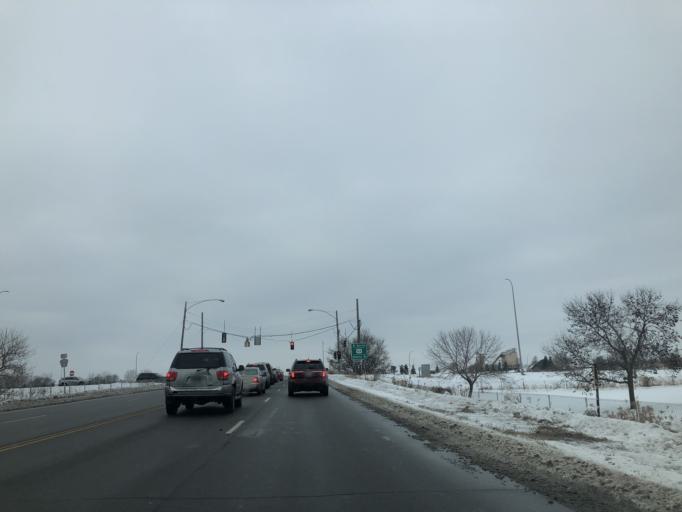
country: US
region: Minnesota
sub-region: Hennepin County
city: Osseo
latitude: 45.0946
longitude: -93.4001
